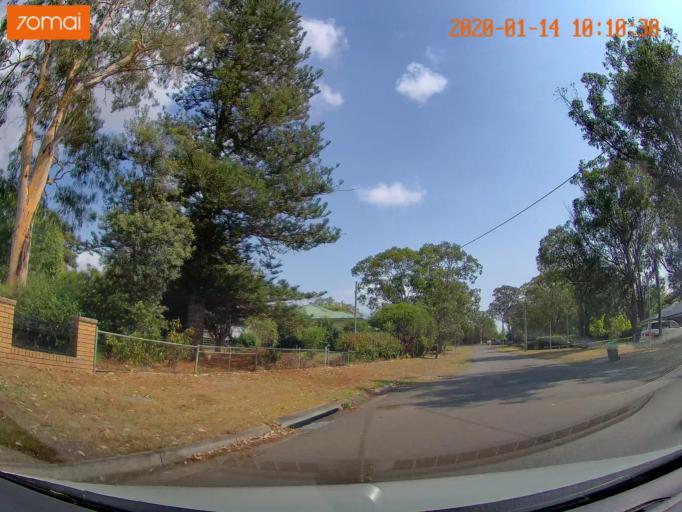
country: AU
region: New South Wales
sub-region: Wyong Shire
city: Kingfisher Shores
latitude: -33.1225
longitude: 151.5358
